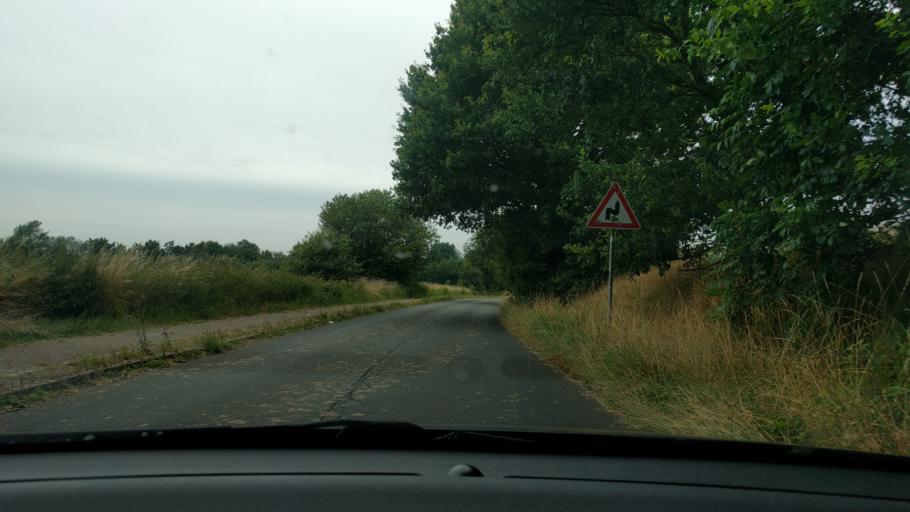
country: DE
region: North Rhine-Westphalia
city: Witten
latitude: 51.4683
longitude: 7.3316
